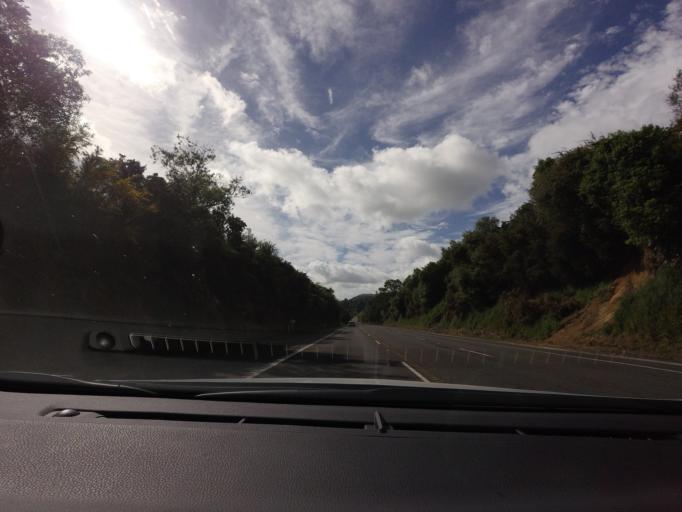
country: NZ
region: Bay of Plenty
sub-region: Rotorua District
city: Rotorua
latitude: -38.0738
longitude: 176.1769
